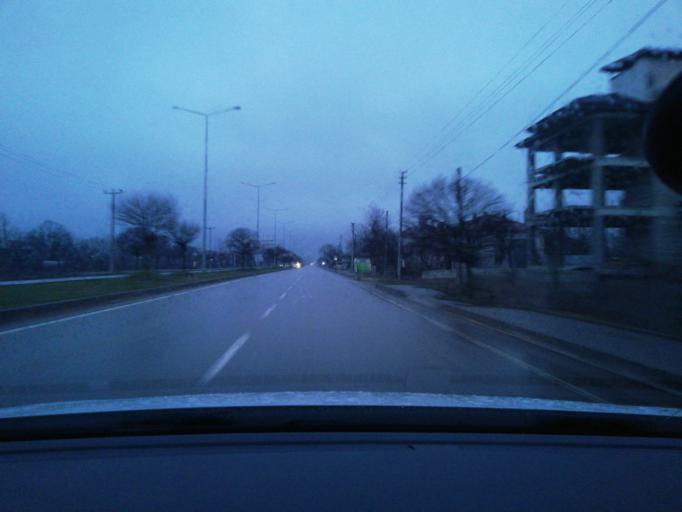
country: TR
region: Bolu
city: Bolu
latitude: 40.7024
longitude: 31.6180
